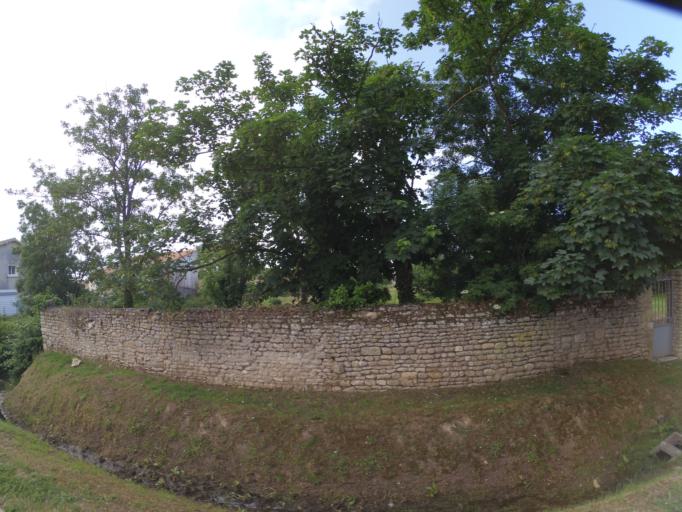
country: FR
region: Poitou-Charentes
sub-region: Departement de la Charente-Maritime
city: Chatelaillon-Plage
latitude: 46.0575
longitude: -1.0786
